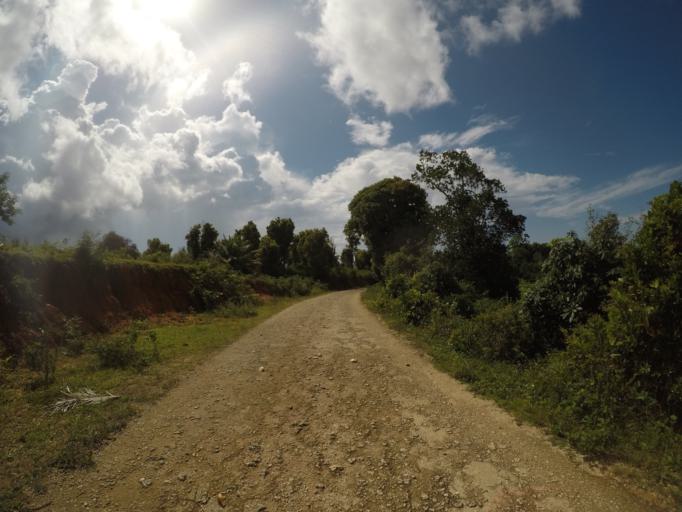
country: TZ
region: Pemba South
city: Mtambile
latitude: -5.3488
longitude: 39.6918
